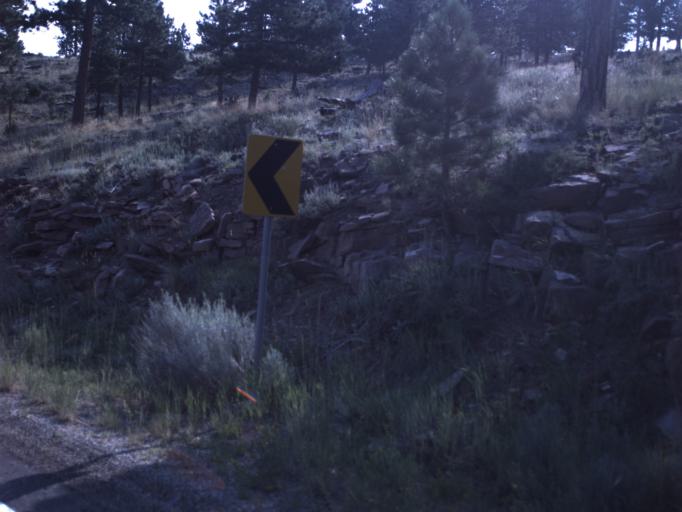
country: US
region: Utah
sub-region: Daggett County
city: Manila
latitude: 40.8958
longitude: -109.4566
